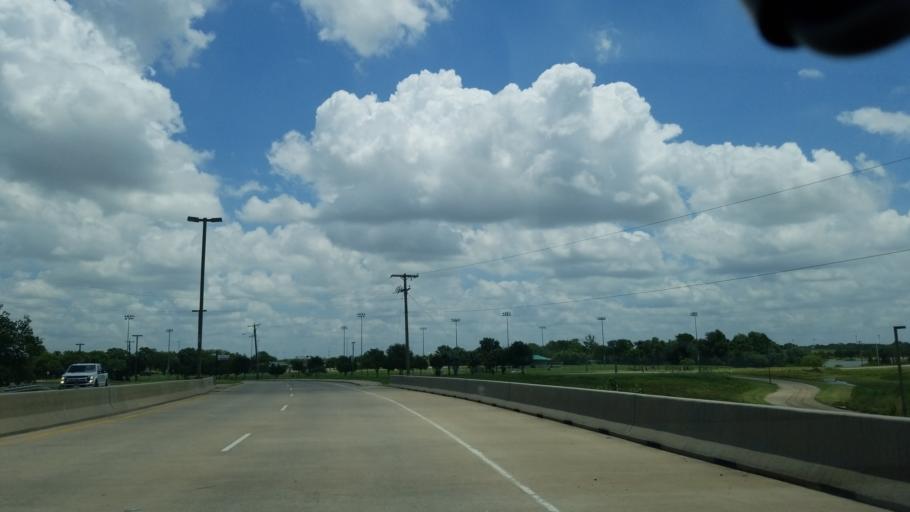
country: US
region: Texas
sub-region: Dallas County
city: Carrollton
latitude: 32.9658
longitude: -96.9423
